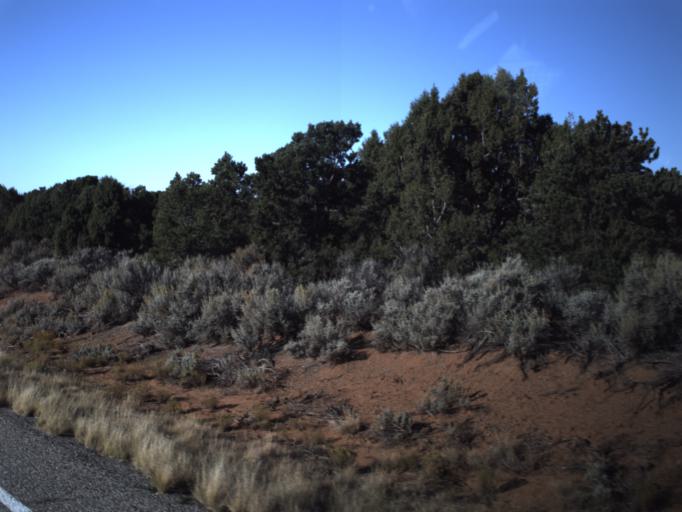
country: US
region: Utah
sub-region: San Juan County
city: Blanding
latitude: 37.5727
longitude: -109.9225
